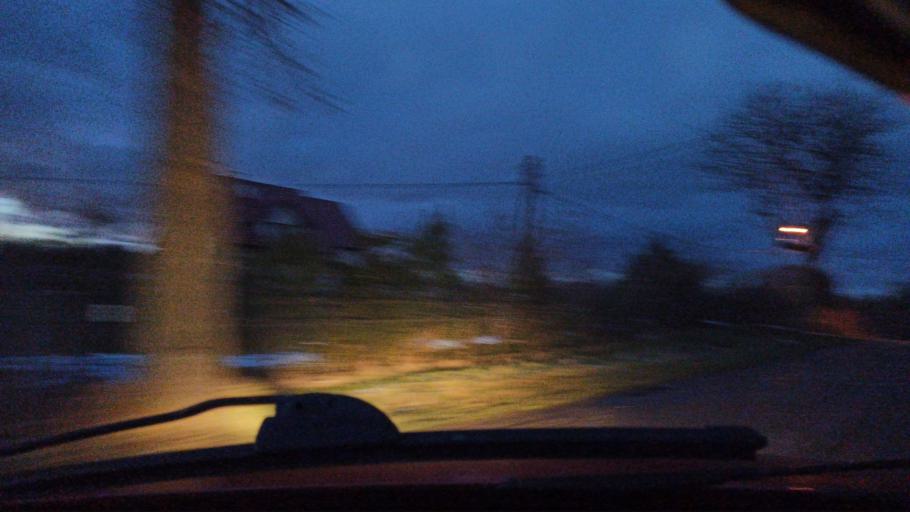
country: PL
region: Warmian-Masurian Voivodeship
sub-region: Powiat elblaski
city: Gronowo Gorne
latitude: 54.1815
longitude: 19.5402
